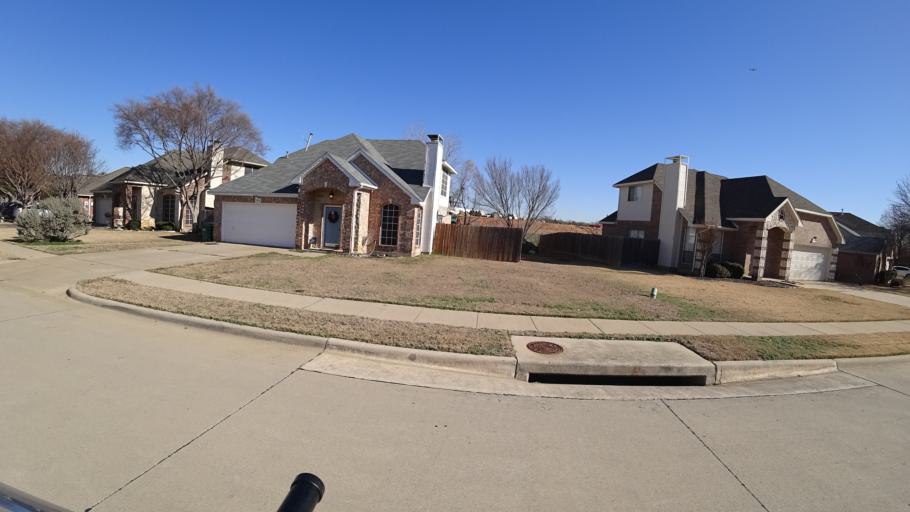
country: US
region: Texas
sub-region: Denton County
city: Lewisville
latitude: 33.0248
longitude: -97.0270
